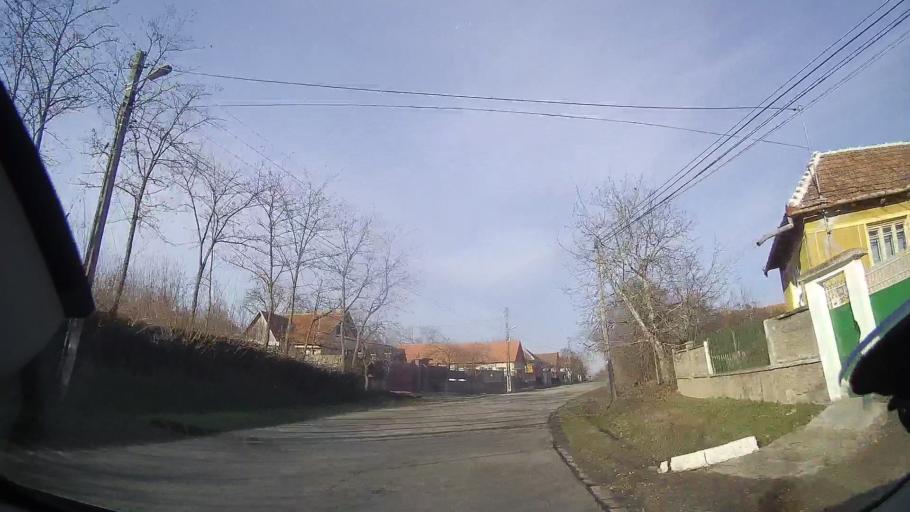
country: RO
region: Bihor
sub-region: Comuna Brusturi
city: Brusturi
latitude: 47.1662
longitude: 22.2207
